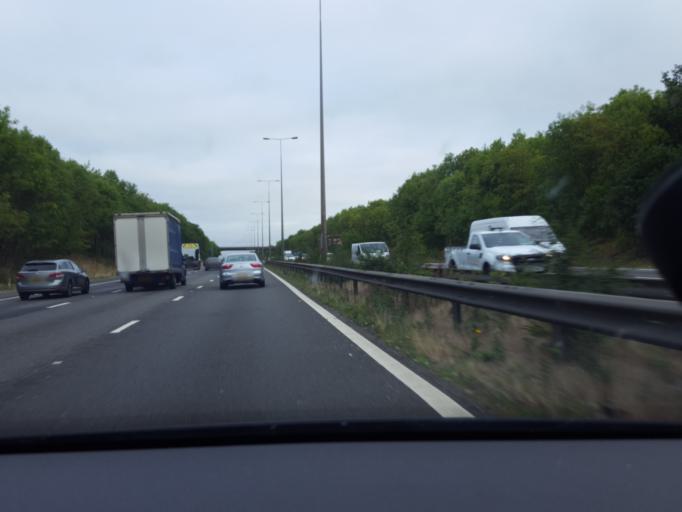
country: GB
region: England
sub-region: Leicestershire
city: Shepshed
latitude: 52.7878
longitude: -1.2867
